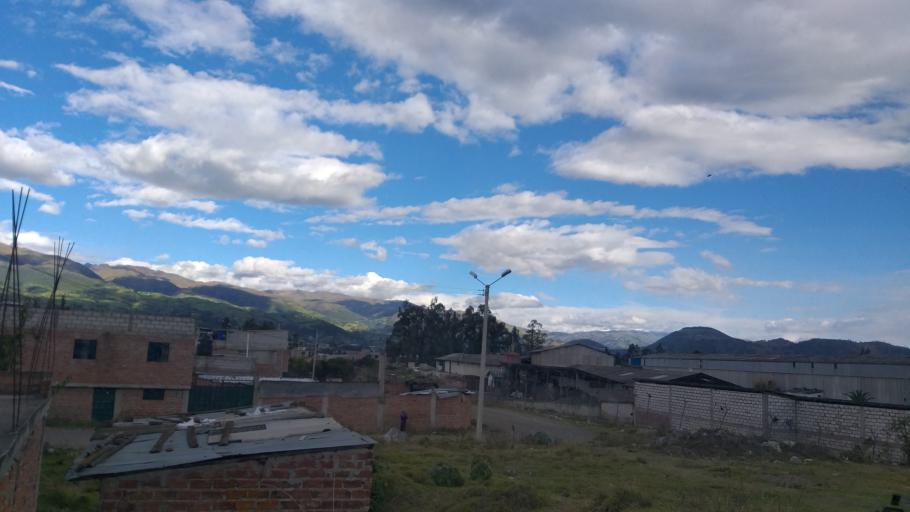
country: EC
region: Chimborazo
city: Riobamba
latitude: -1.6886
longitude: -78.6301
